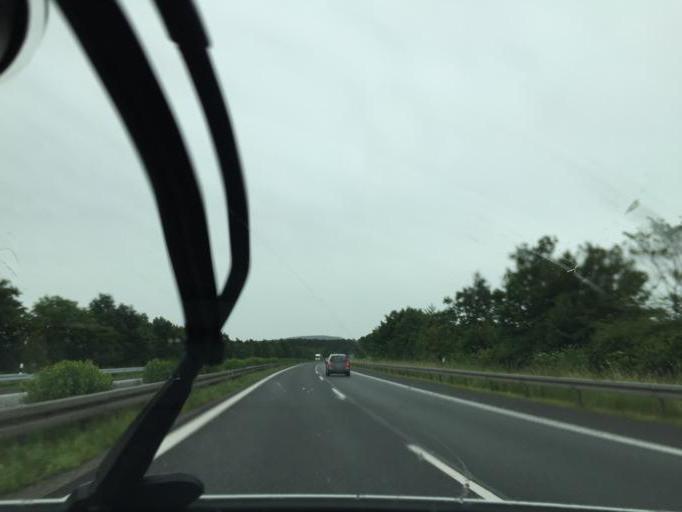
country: DE
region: Bavaria
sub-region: Regierungsbezirk Unterfranken
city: Hassfurt
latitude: 50.0015
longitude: 10.5121
